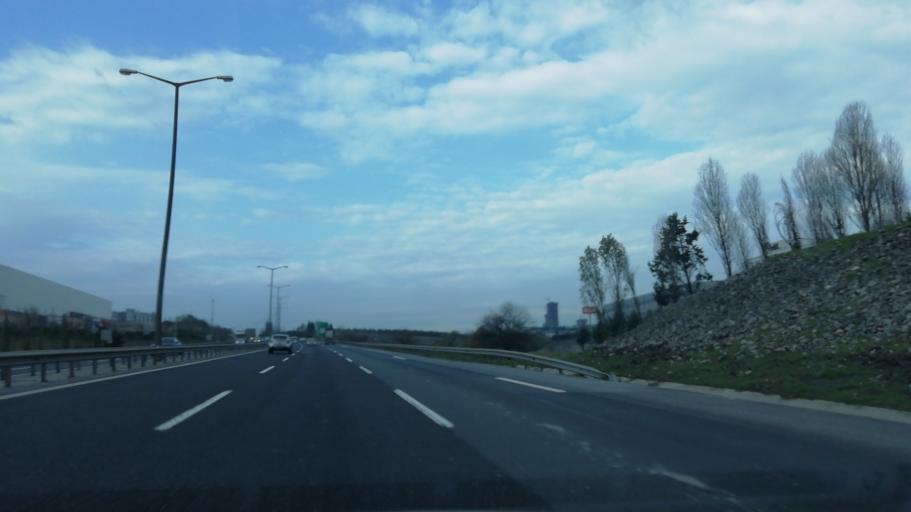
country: TR
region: Istanbul
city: Esenyurt
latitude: 41.0739
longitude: 28.6473
